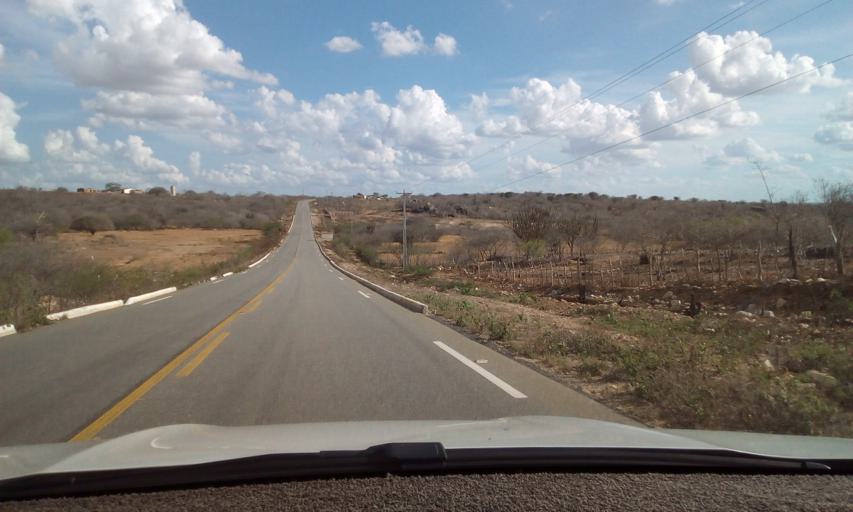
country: BR
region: Paraiba
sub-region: Soledade
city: Soledade
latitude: -6.7978
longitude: -36.4052
